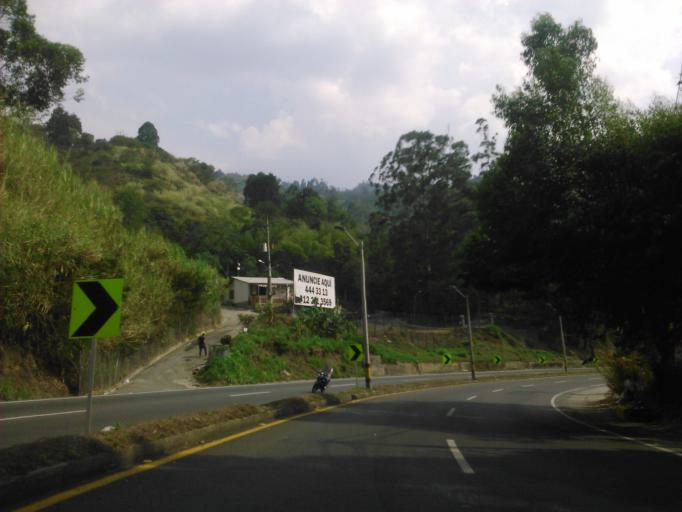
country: CO
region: Antioquia
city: Bello
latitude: 6.3183
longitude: -75.5296
